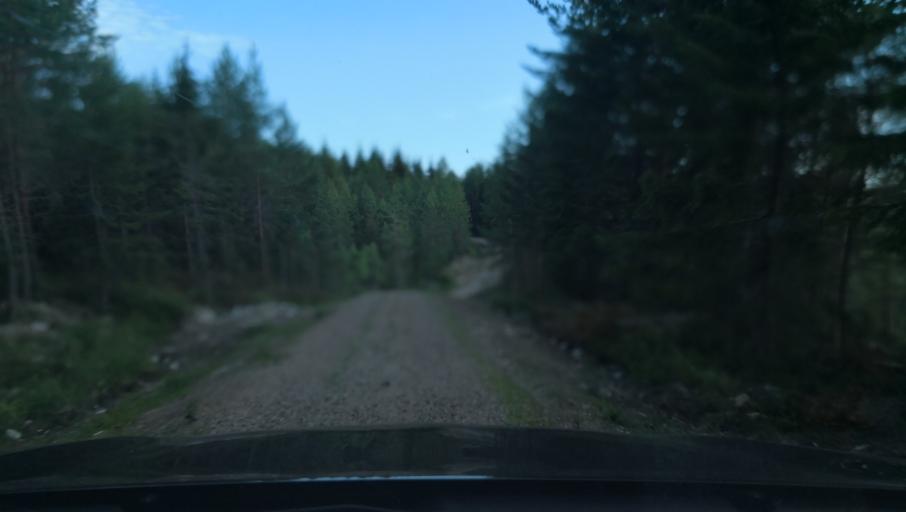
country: SE
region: Dalarna
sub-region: Smedjebackens Kommun
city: Smedjebacken
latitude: 60.0654
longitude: 15.3087
